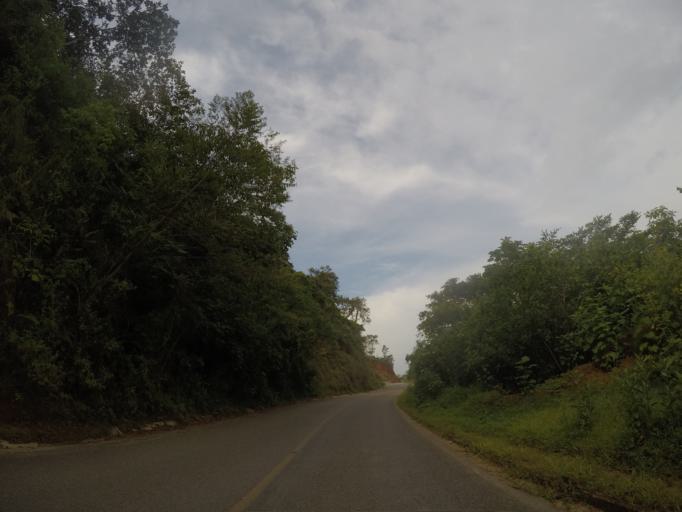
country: MX
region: Oaxaca
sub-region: San Pedro Pochutla
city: Los Naranjos Esquipulas
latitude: 15.9600
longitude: -96.4567
